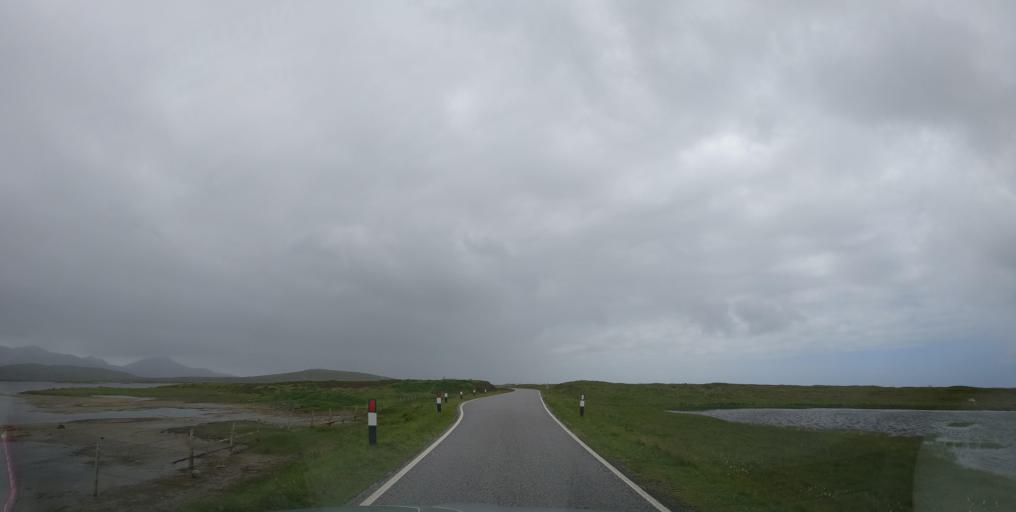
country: GB
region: Scotland
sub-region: Eilean Siar
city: Benbecula
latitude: 57.3651
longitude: -7.3529
